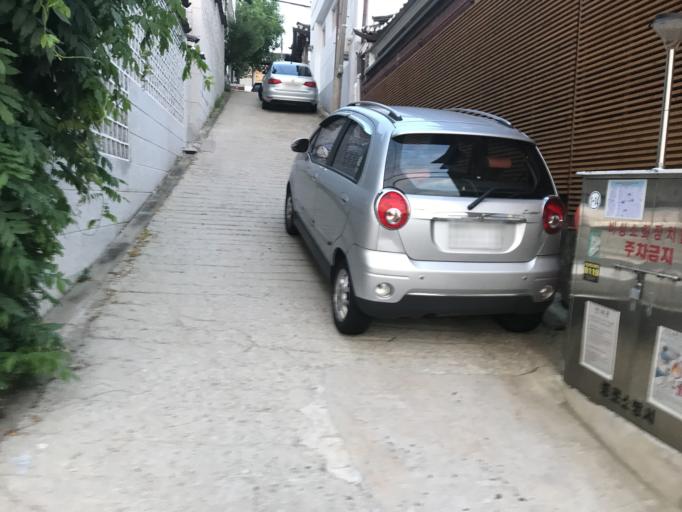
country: KR
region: Seoul
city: Seoul
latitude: 37.5831
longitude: 126.9823
